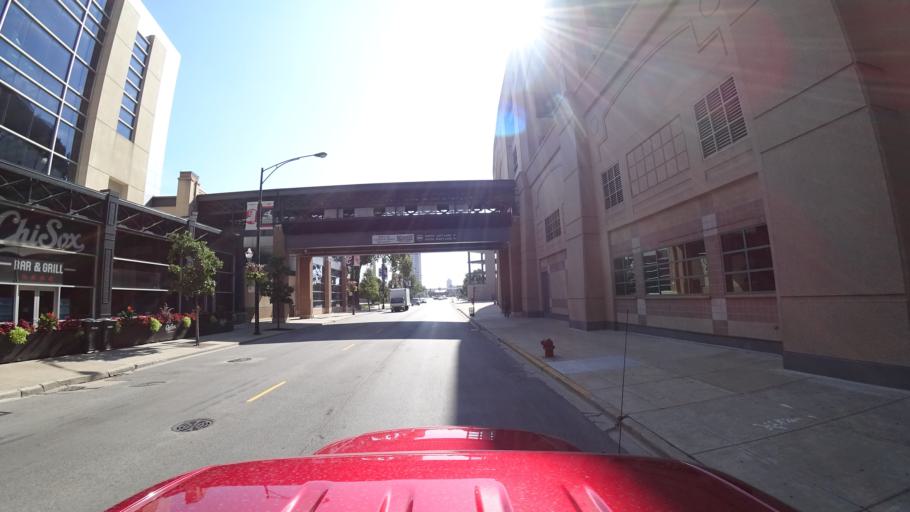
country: US
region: Illinois
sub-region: Cook County
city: Chicago
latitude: 41.8309
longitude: -87.6341
